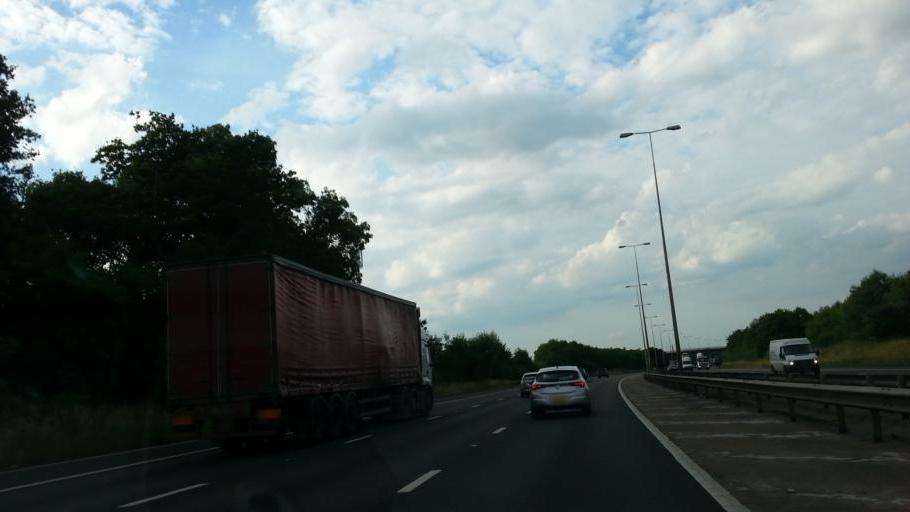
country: GB
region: England
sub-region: Worcestershire
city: Kempsey
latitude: 52.1289
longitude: -2.2010
